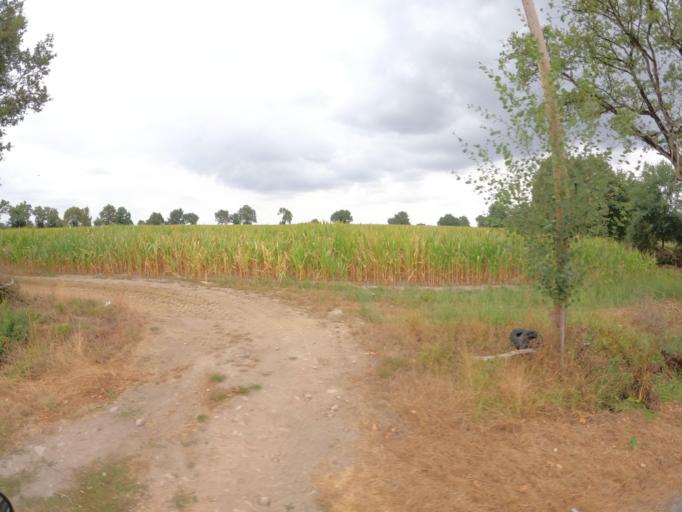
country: FR
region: Pays de la Loire
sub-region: Departement de la Vendee
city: Tiffauges
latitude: 46.9976
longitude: -1.0928
